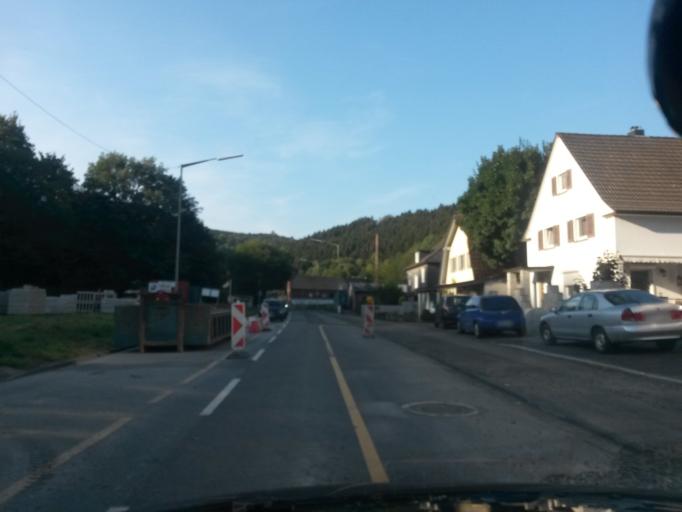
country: DE
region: North Rhine-Westphalia
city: Bergneustadt
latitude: 51.0149
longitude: 7.6234
